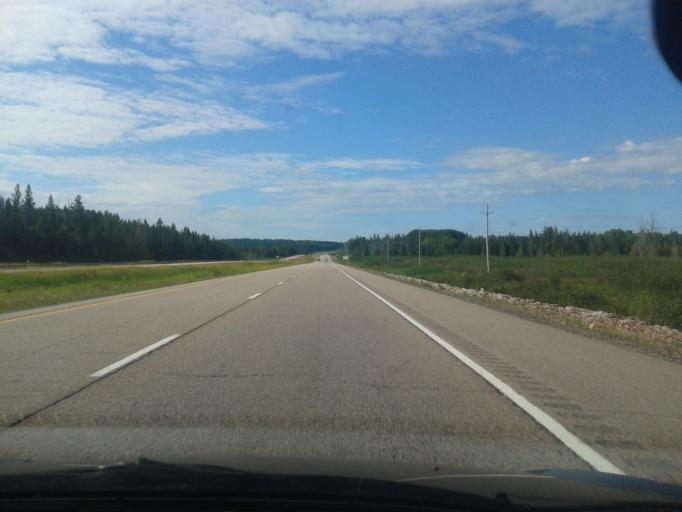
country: CA
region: Ontario
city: South River
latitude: 45.9315
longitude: -79.3650
